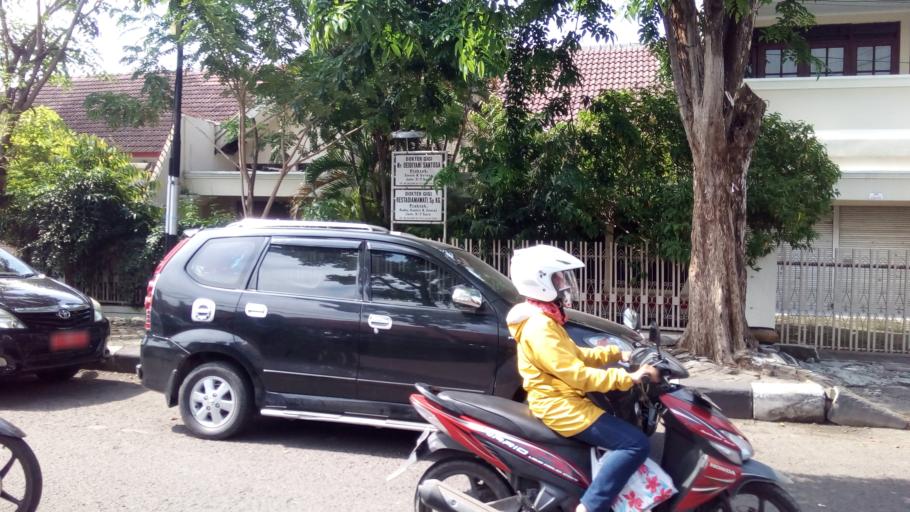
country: ID
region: Central Java
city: Semarang
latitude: -7.0055
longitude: 110.4356
